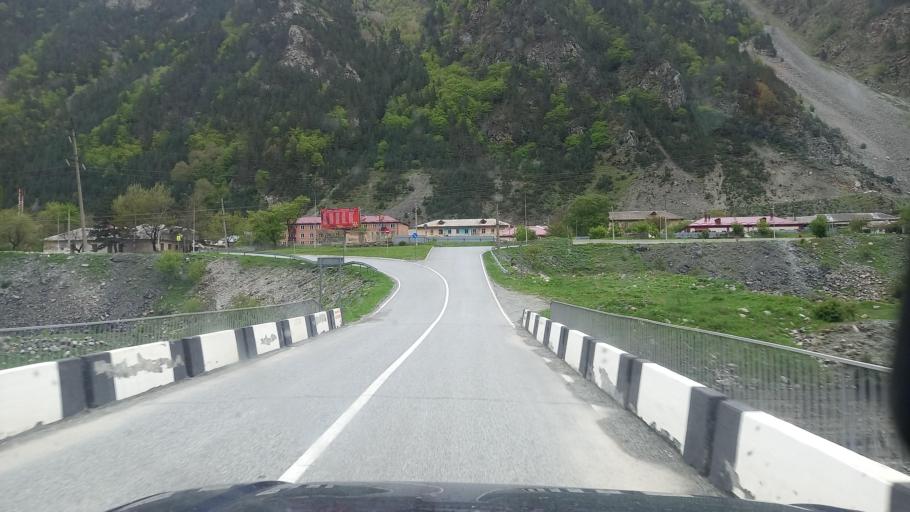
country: RU
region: North Ossetia
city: Mizur
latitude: 42.7945
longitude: 44.0047
